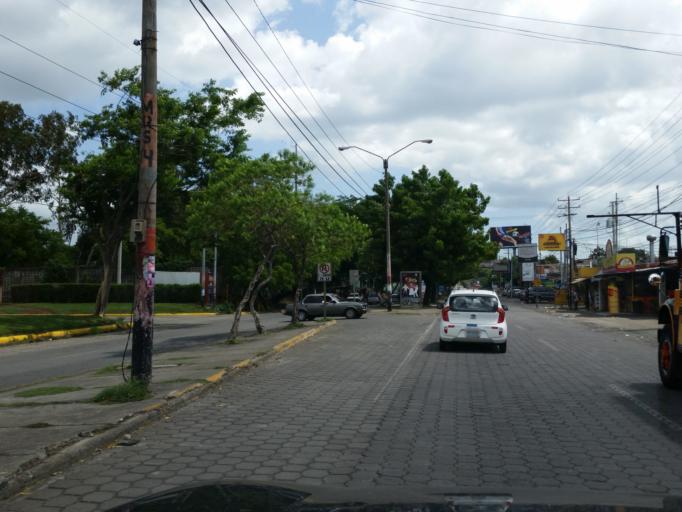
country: NI
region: Managua
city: Managua
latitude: 12.1183
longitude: -86.2493
